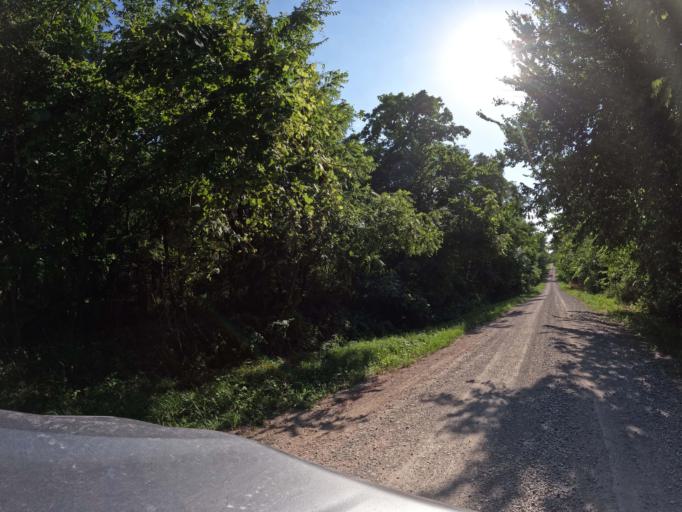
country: US
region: Iowa
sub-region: Appanoose County
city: Centerville
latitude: 40.7321
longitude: -93.0166
